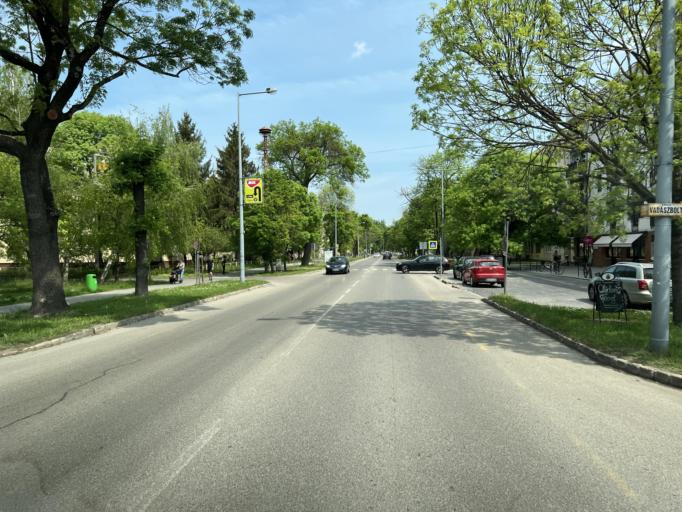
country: HU
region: Pest
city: Nagykoros
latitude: 47.0369
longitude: 19.7844
